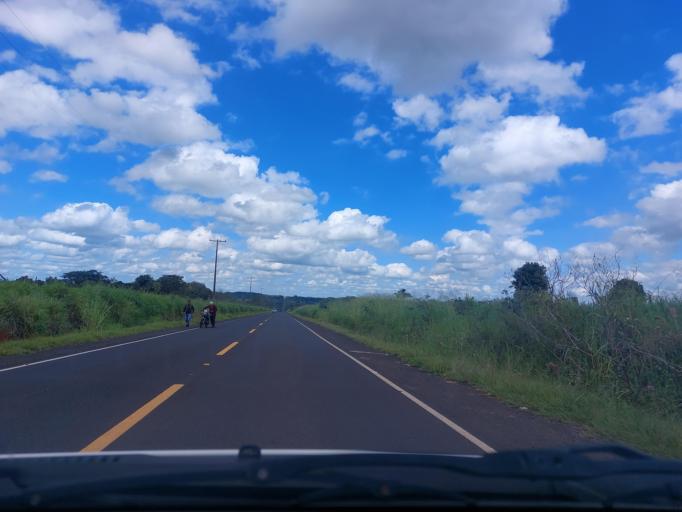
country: PY
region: San Pedro
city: Guayaybi
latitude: -24.5363
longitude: -56.5197
